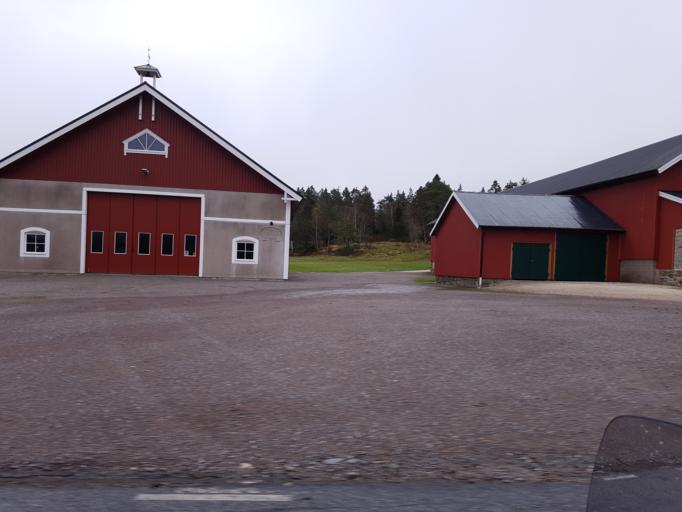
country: SE
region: Vaestra Goetaland
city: Svanesund
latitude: 58.1713
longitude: 11.7833
